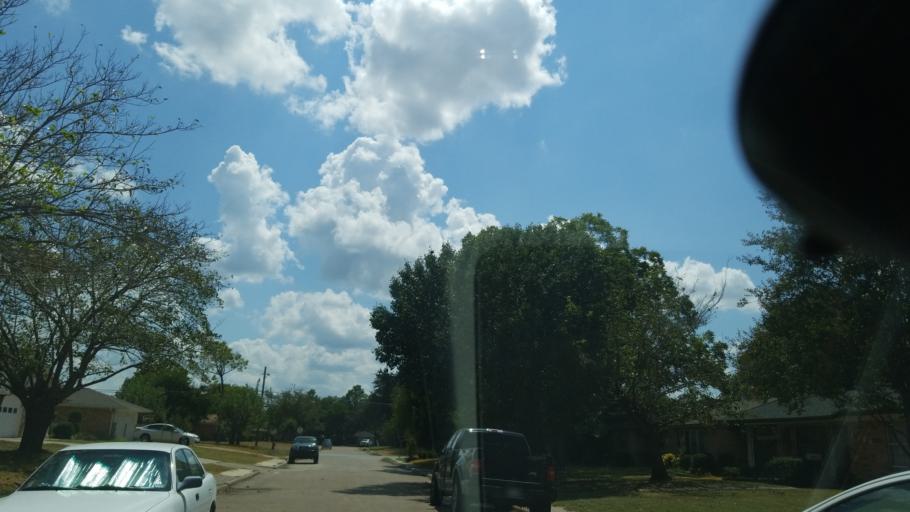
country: US
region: Texas
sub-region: Dallas County
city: Grand Prairie
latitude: 32.7214
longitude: -96.9964
